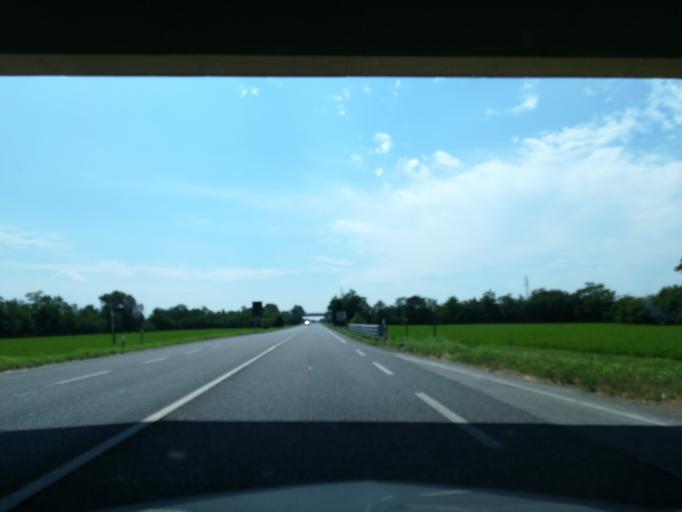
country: IT
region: Lombardy
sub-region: Provincia di Bergamo
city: Grassobbio
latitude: 45.6362
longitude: 9.7112
